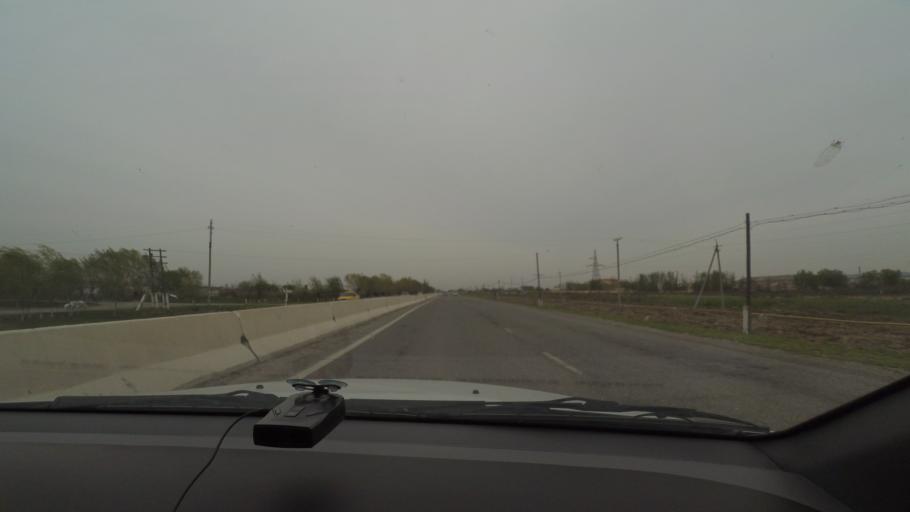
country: UZ
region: Sirdaryo
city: Guliston
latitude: 40.4901
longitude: 68.7233
